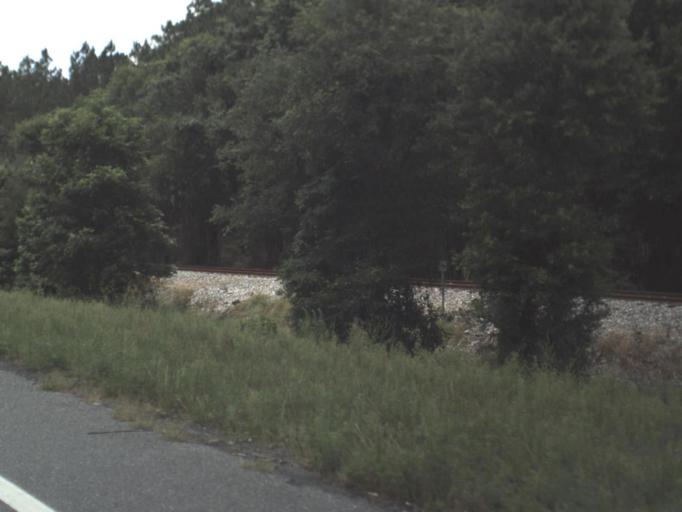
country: US
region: Florida
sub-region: Suwannee County
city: Wellborn
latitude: 30.3220
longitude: -82.7309
